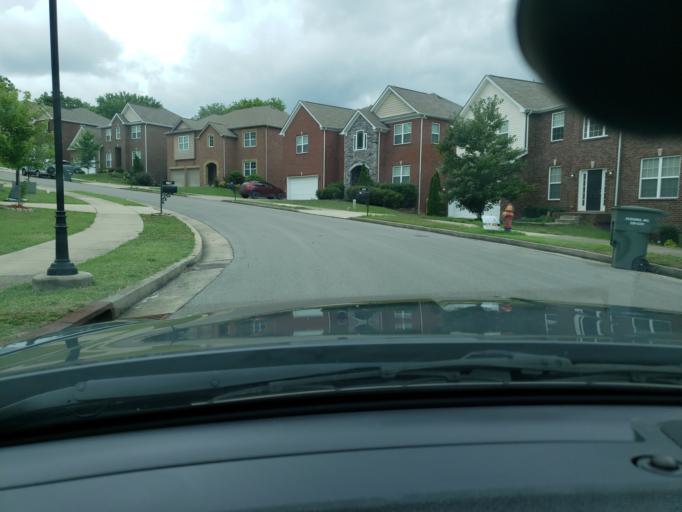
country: US
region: Tennessee
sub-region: Williamson County
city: Nolensville
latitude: 36.0252
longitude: -86.6987
